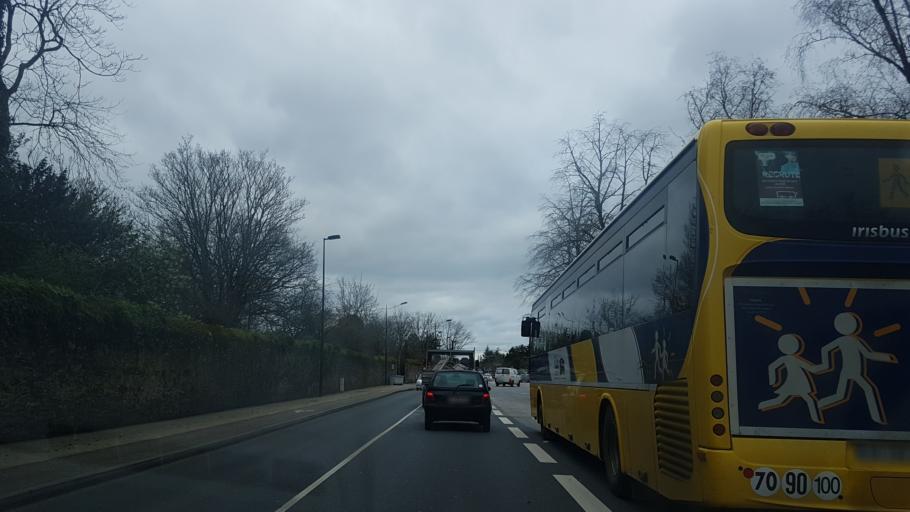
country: FR
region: Pays de la Loire
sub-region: Departement de la Loire-Atlantique
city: Nantes
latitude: 47.2518
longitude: -1.5300
